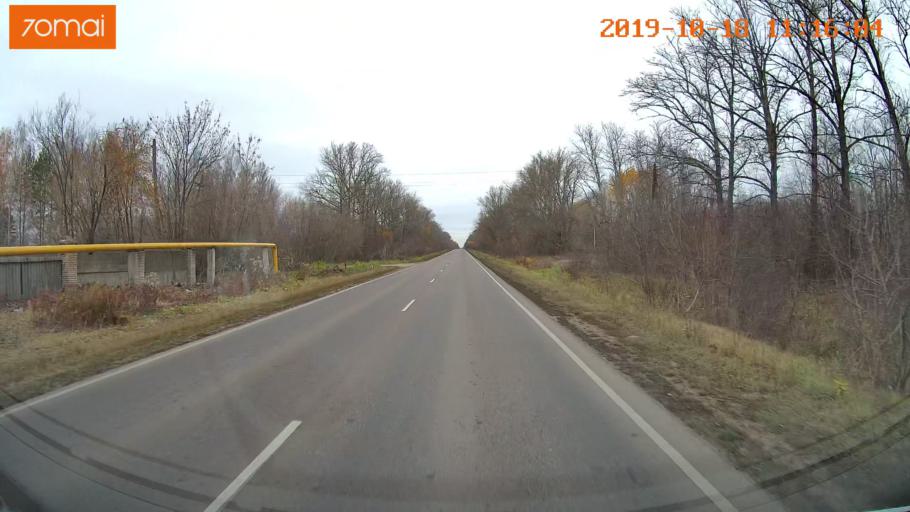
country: RU
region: Tula
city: Kimovsk
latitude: 54.0019
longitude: 38.5482
